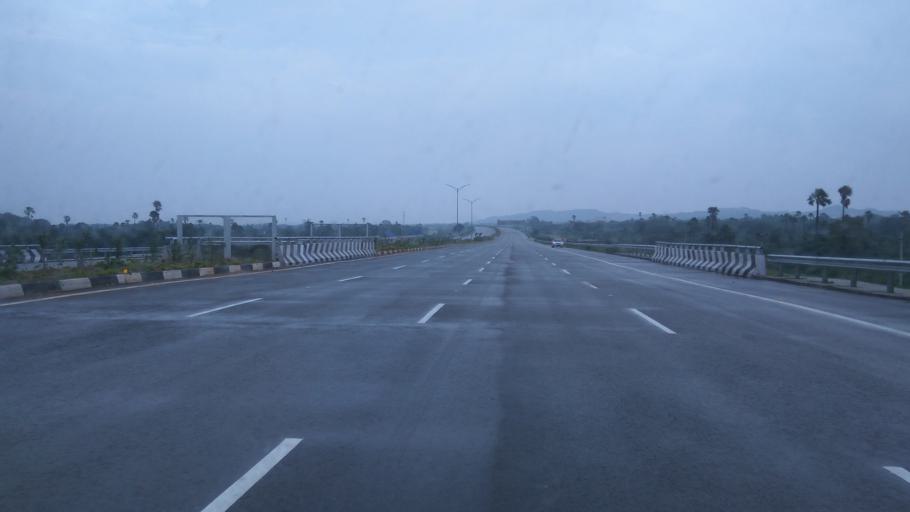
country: IN
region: Telangana
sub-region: Rangareddi
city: Ghatkesar
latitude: 17.4561
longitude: 78.6693
